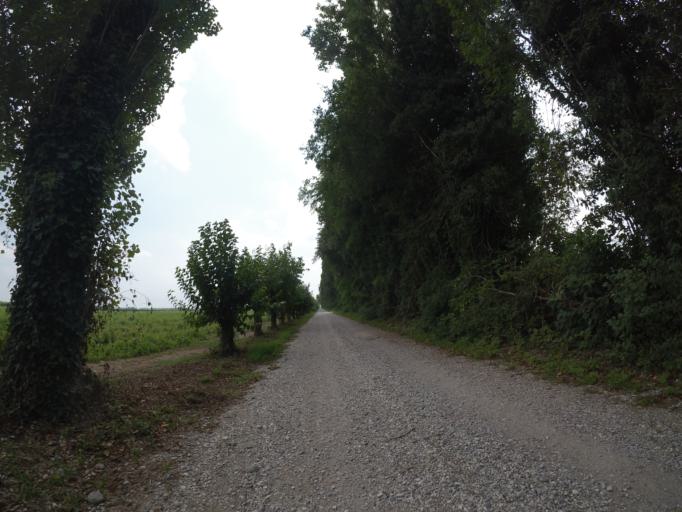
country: IT
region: Friuli Venezia Giulia
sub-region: Provincia di Udine
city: Sedegliano
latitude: 46.0052
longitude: 13.0107
